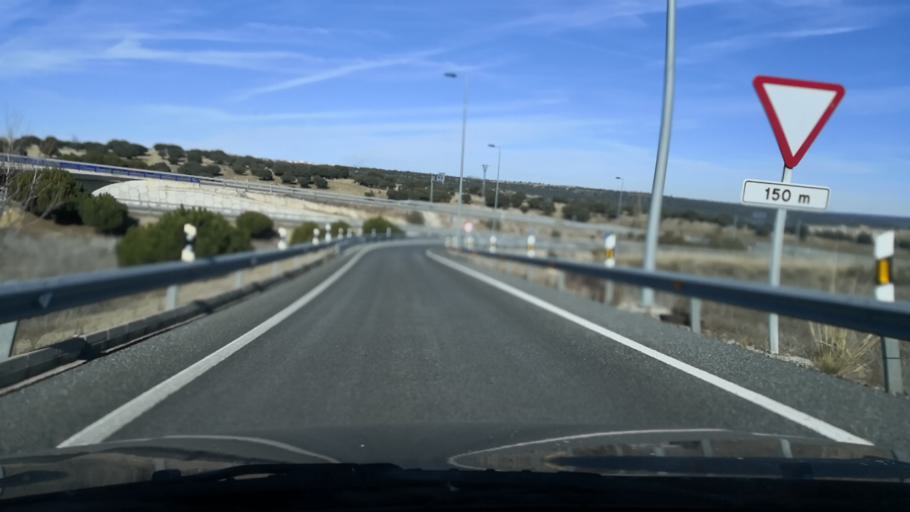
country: ES
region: Castille and Leon
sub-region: Provincia de Avila
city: Avila
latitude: 40.6676
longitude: -4.7147
